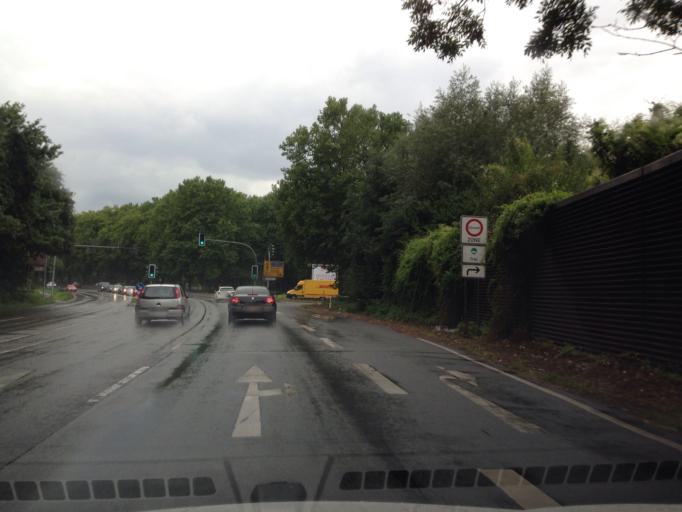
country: DE
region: North Rhine-Westphalia
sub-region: Regierungsbezirk Munster
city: Gladbeck
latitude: 51.5662
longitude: 6.9885
